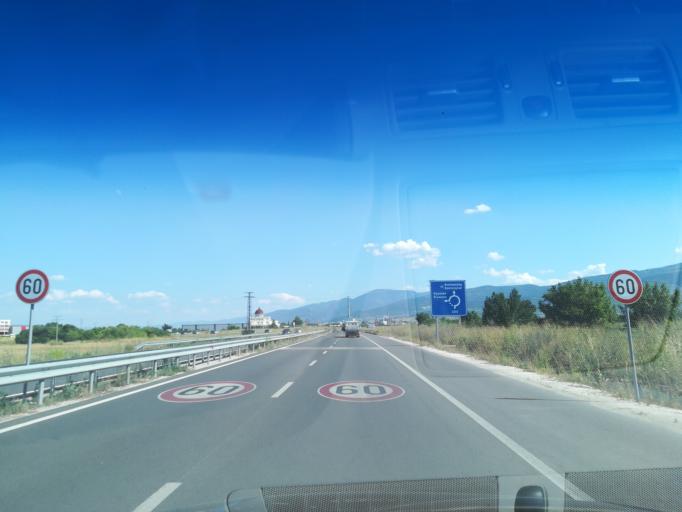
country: BG
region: Plovdiv
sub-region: Obshtina Plovdiv
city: Plovdiv
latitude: 42.0826
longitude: 24.7992
